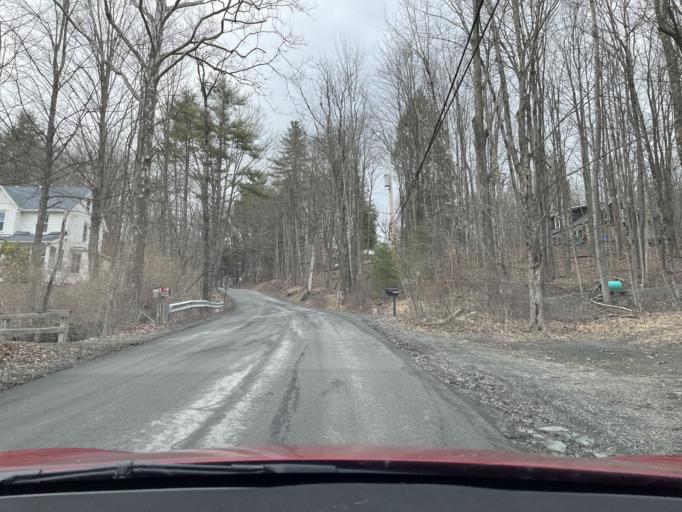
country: US
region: New York
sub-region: Ulster County
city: Woodstock
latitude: 42.0668
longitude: -74.1589
